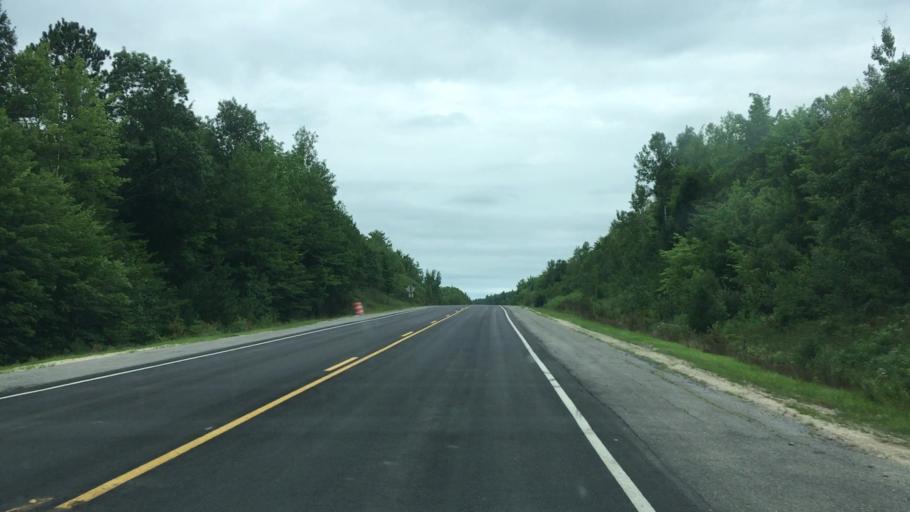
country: US
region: Maine
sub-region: Washington County
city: Cherryfield
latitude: 44.8868
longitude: -67.8568
